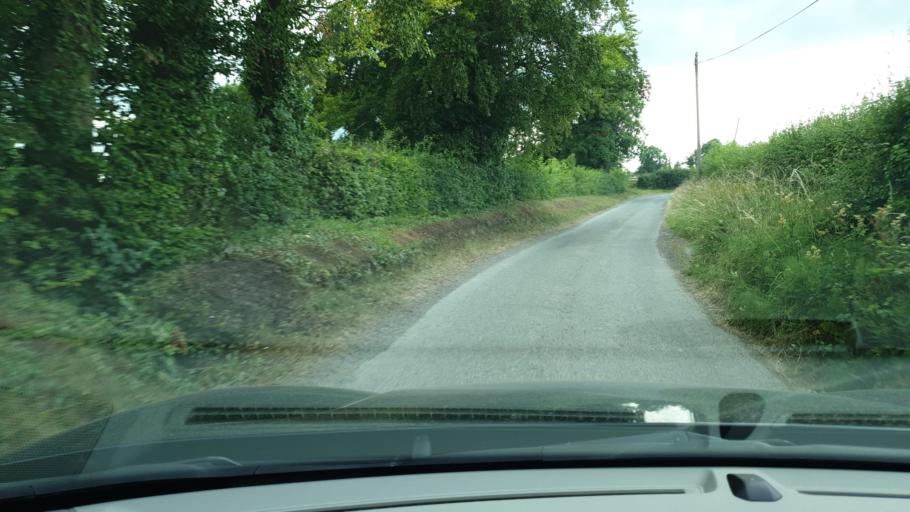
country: IE
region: Leinster
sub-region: An Mhi
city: Ratoath
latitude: 53.4696
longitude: -6.4571
